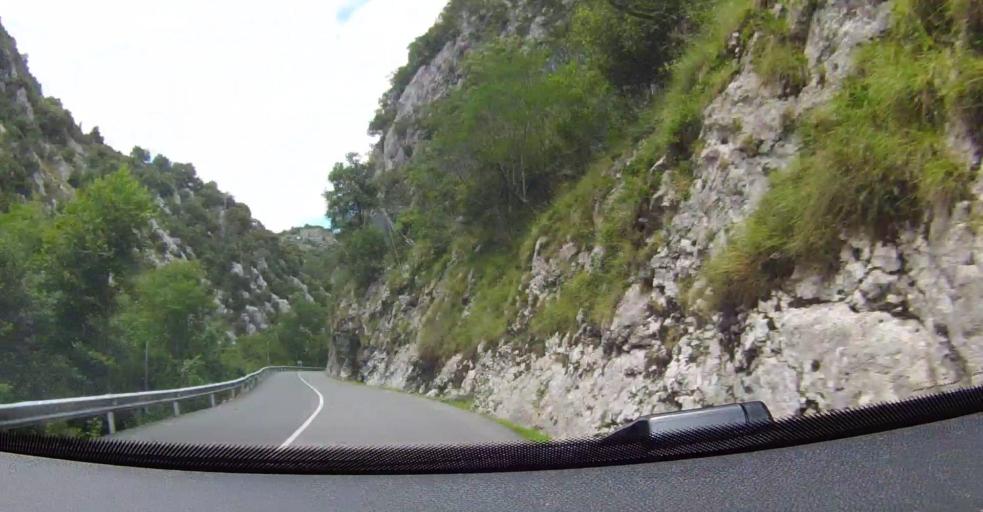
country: ES
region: Cantabria
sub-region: Provincia de Cantabria
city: Tresviso
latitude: 43.3073
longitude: -4.6058
